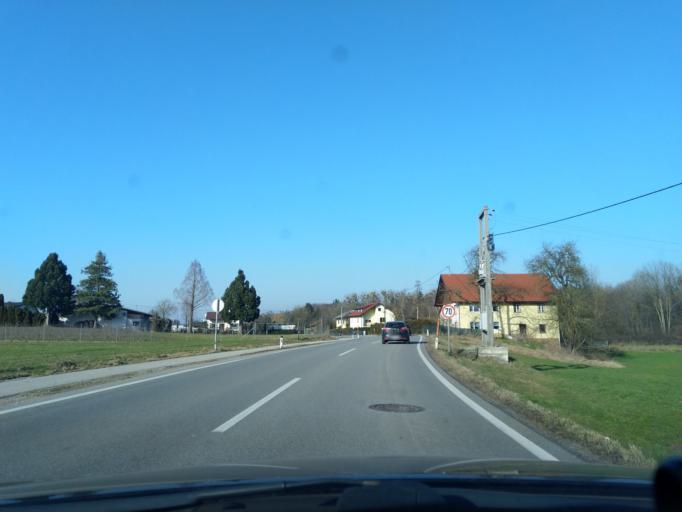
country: AT
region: Upper Austria
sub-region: Politischer Bezirk Ried im Innkreis
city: Ried im Innkreis
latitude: 48.2782
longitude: 13.4459
